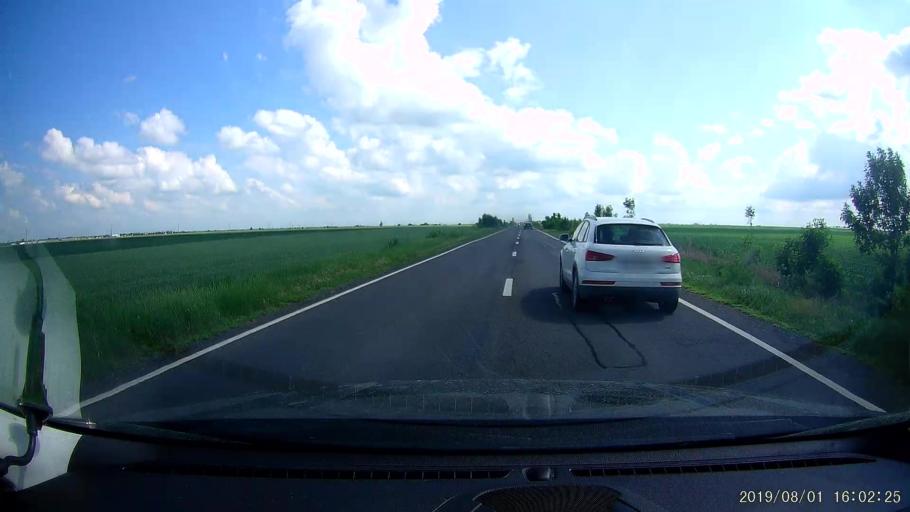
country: RO
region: Ialomita
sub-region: Comuna Ciulnita
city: Ciulnita
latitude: 44.4898
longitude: 27.3873
